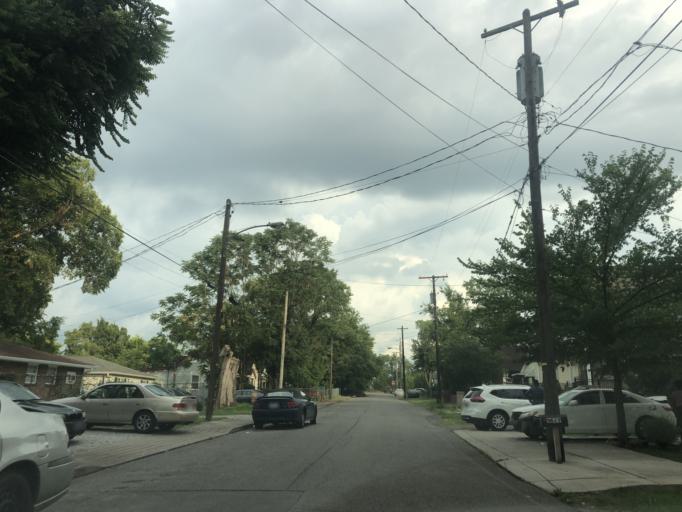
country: US
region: Tennessee
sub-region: Davidson County
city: Nashville
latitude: 36.1758
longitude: -86.8027
